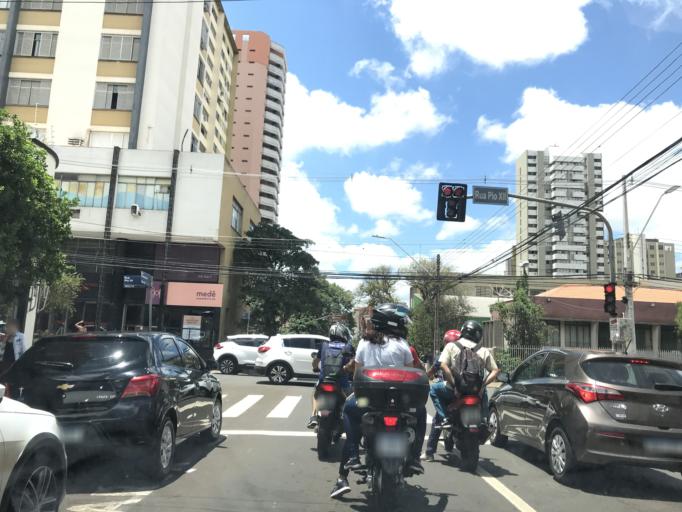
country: BR
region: Parana
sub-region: Londrina
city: Londrina
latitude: -23.3119
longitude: -51.1628
